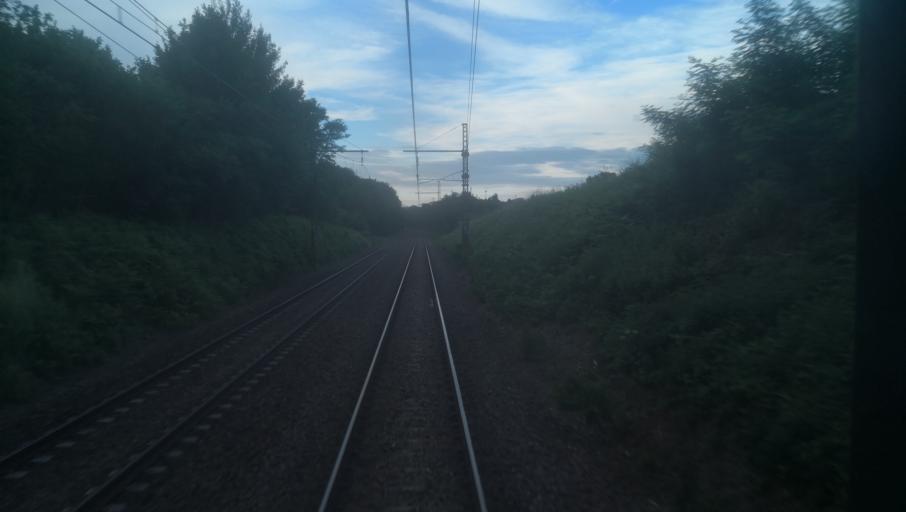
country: FR
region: Limousin
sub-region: Departement de la Creuse
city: La Souterraine
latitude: 46.2092
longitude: 1.4800
